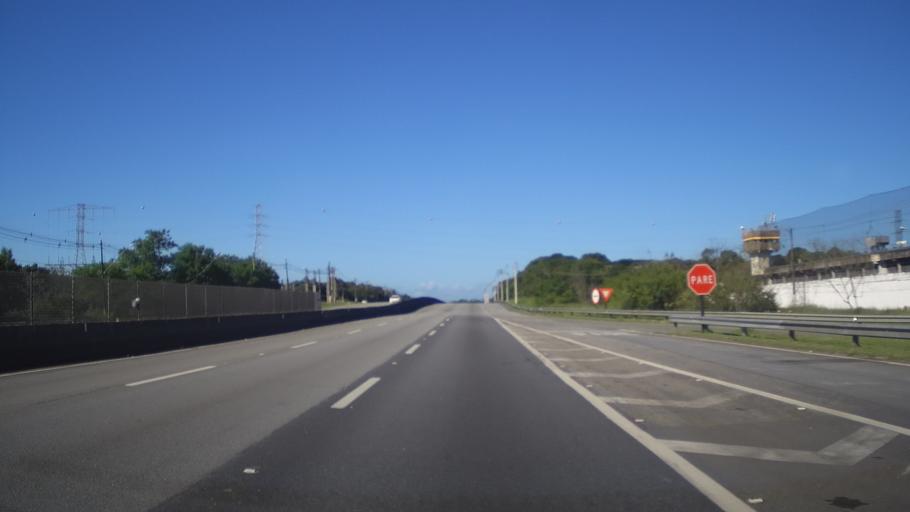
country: BR
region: Sao Paulo
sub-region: Sao Vicente
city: Sao Vicente
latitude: -23.9623
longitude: -46.4704
